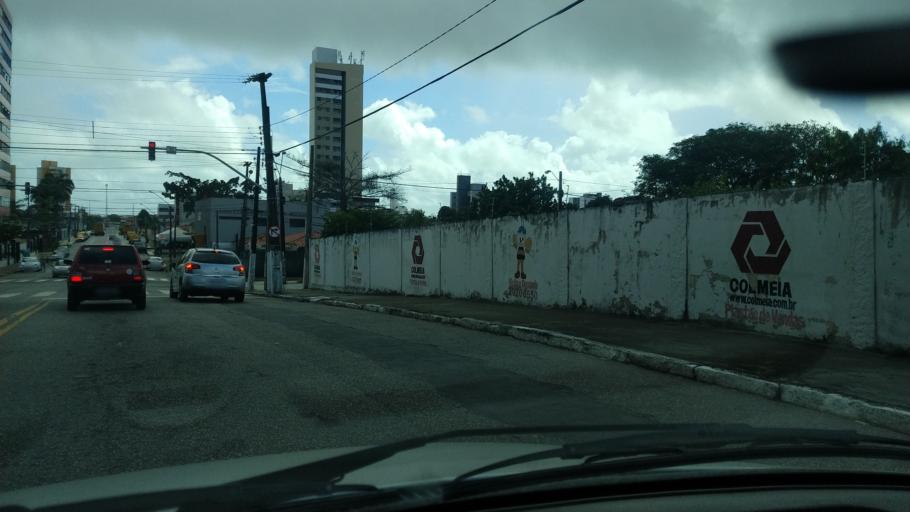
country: BR
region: Rio Grande do Norte
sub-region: Natal
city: Natal
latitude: -5.8139
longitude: -35.2197
